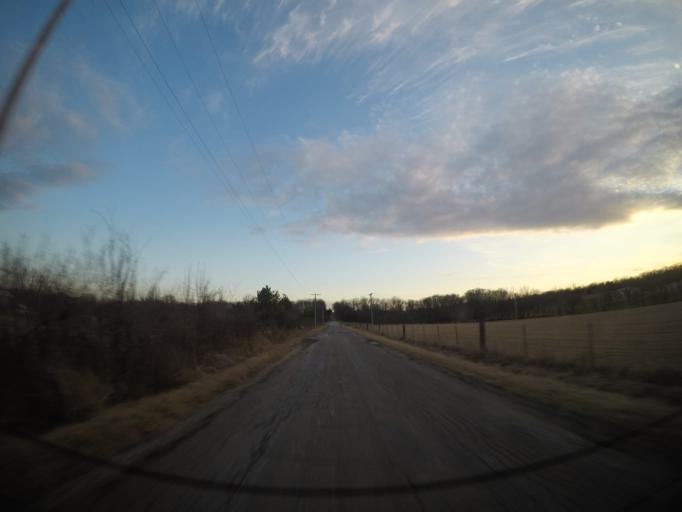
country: US
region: Kansas
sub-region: Wyandotte County
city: Bonner Springs
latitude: 39.0321
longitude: -94.9089
